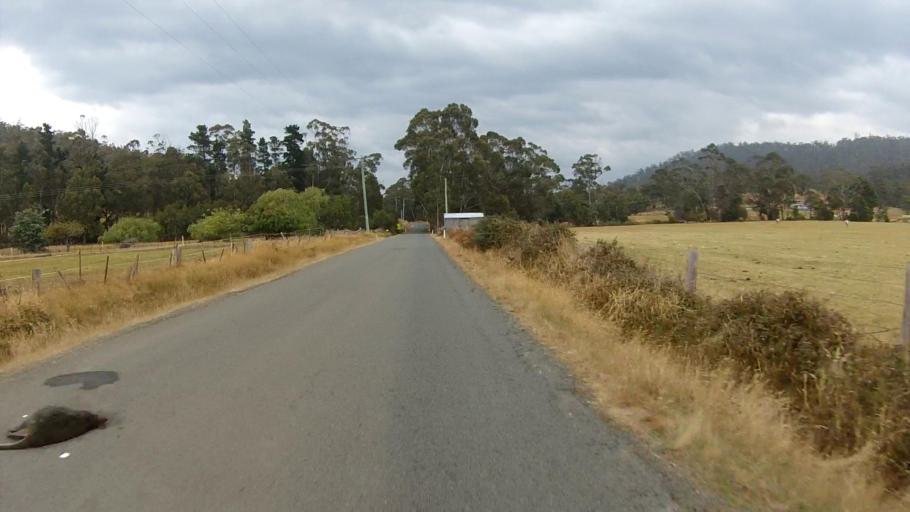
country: AU
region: Tasmania
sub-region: Huon Valley
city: Cygnet
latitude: -43.2388
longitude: 147.1539
